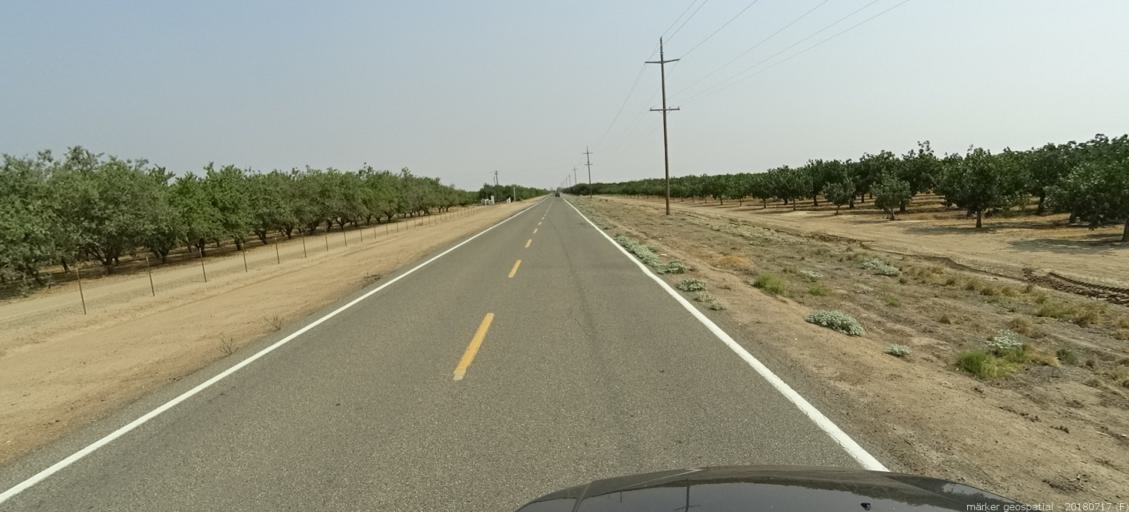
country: US
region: California
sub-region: Madera County
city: Fairmead
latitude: 37.1113
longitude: -120.1470
